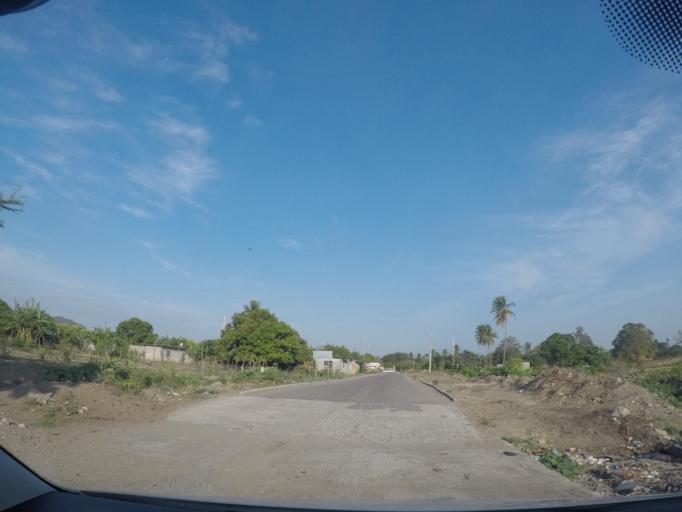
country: MX
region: Oaxaca
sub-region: Santo Domingo Tehuantepec
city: La Noria
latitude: 16.2480
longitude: -95.1469
